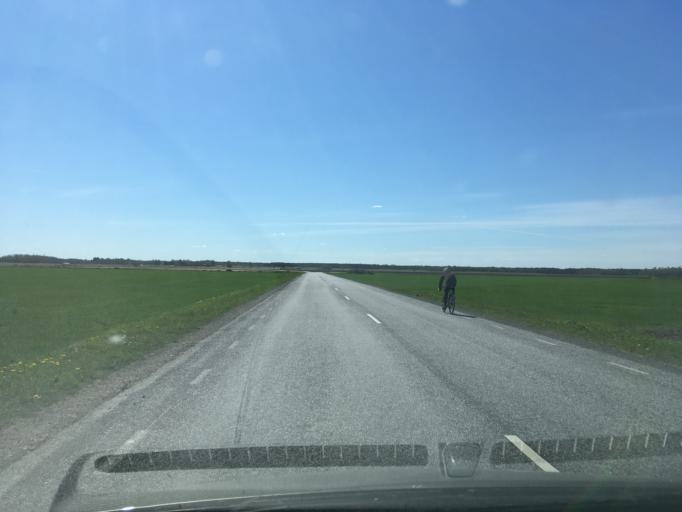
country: EE
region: Harju
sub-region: Raasiku vald
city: Arukula
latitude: 59.4289
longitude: 25.0797
